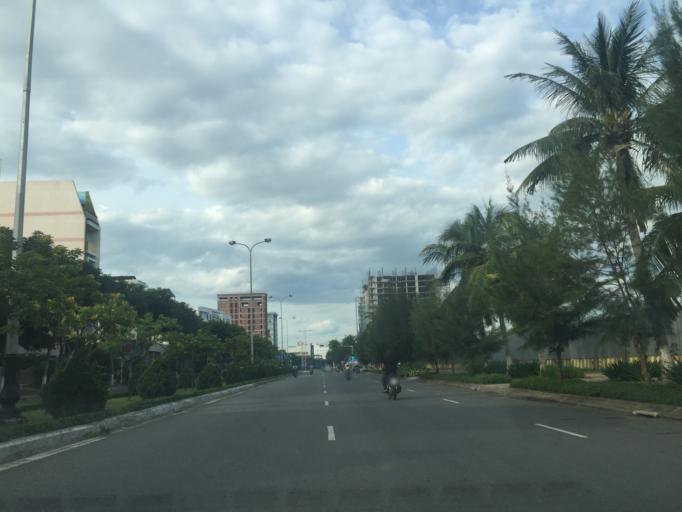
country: VN
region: Da Nang
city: Da Nang
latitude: 16.0816
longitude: 108.2119
